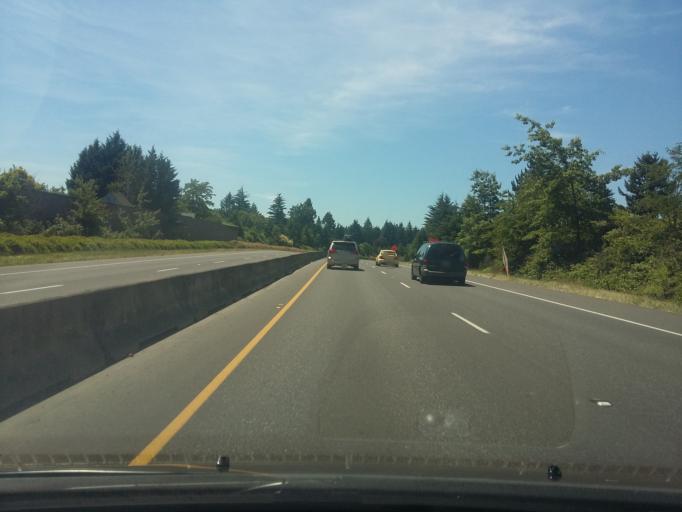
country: US
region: Washington
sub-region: Clark County
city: Five Corners
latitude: 45.6822
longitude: -122.5649
